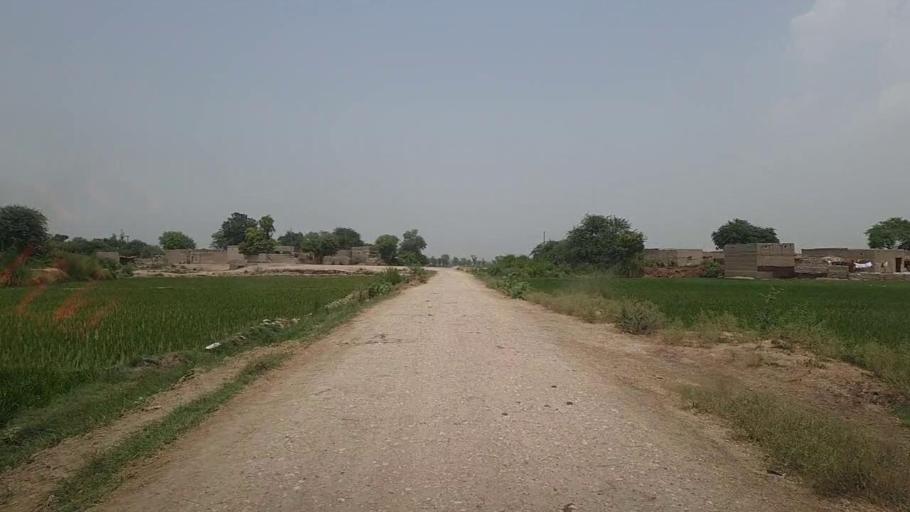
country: PK
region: Sindh
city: Sita Road
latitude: 27.0816
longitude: 67.8737
